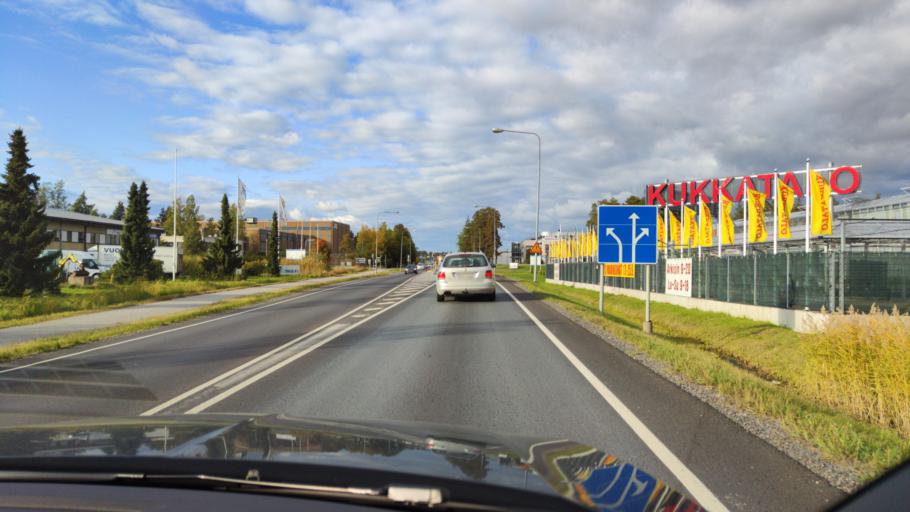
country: FI
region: Varsinais-Suomi
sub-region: Turku
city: Kaarina
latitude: 60.4152
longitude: 22.3838
